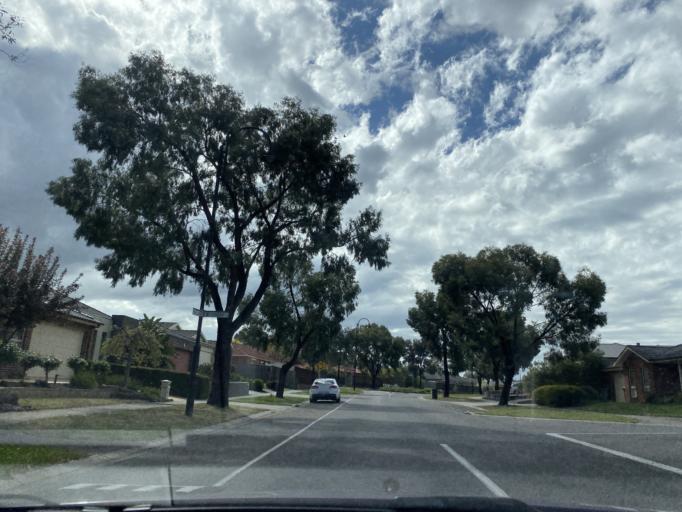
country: AU
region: Victoria
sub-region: Whittlesea
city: Mernda
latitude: -37.6252
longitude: 145.0928
